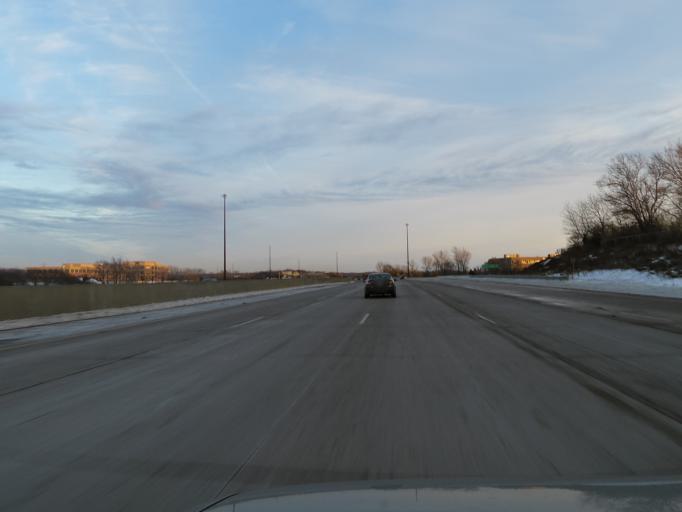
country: US
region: Minnesota
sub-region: Hennepin County
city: Eden Prairie
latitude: 44.8610
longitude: -93.4212
